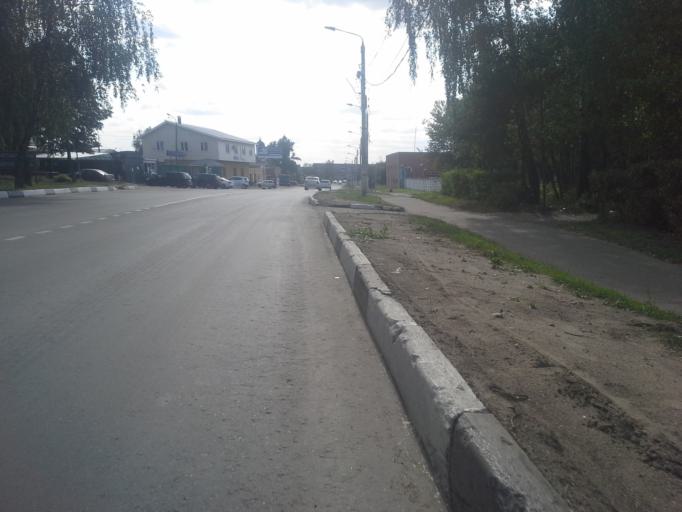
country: RU
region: Moskovskaya
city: Aprelevka
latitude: 55.5478
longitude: 37.0801
